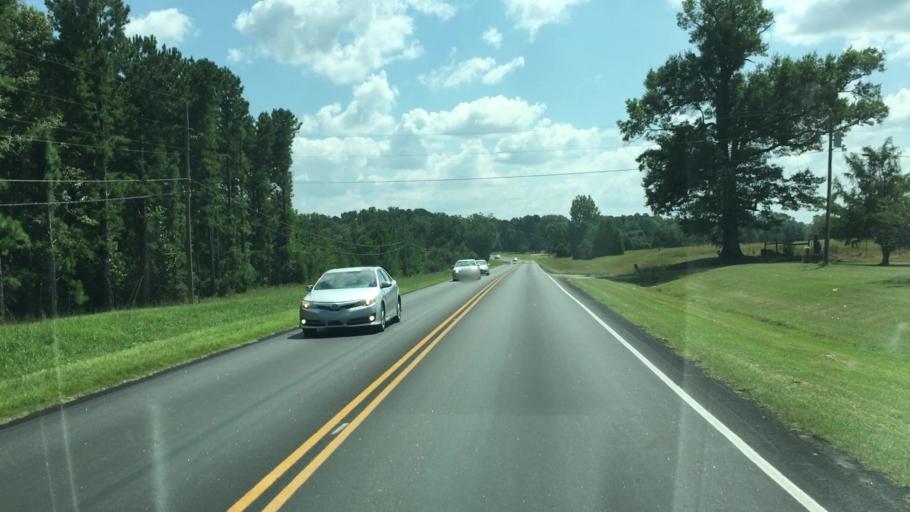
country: US
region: Georgia
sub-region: Morgan County
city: Madison
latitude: 33.6238
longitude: -83.4506
